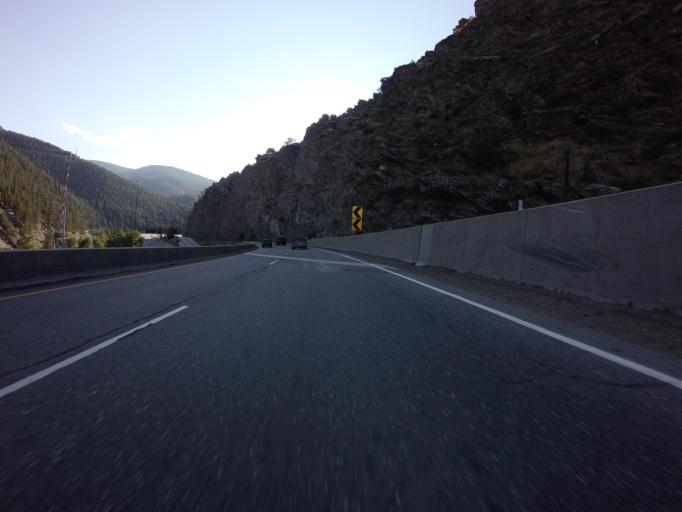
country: US
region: Colorado
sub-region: Clear Creek County
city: Idaho Springs
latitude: 39.7459
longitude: -105.4388
